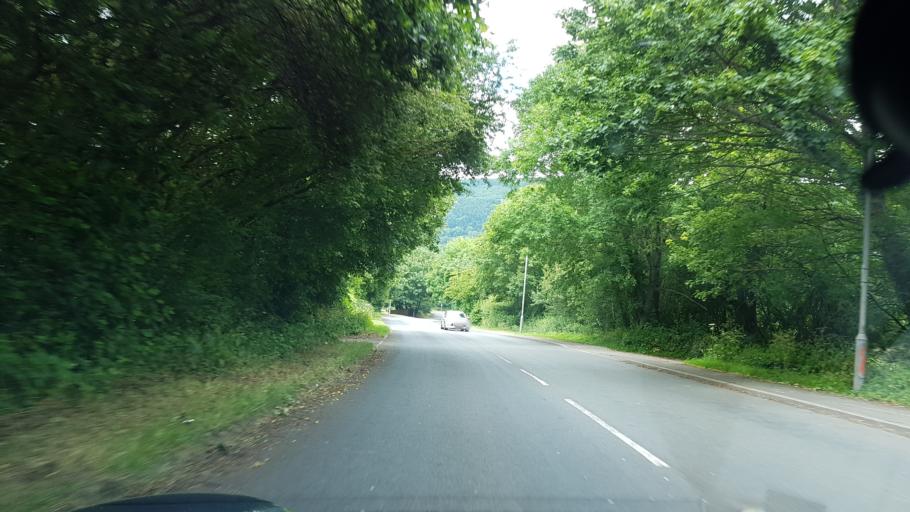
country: GB
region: Wales
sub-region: Monmouthshire
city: Gilwern
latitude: 51.8255
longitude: -3.0818
